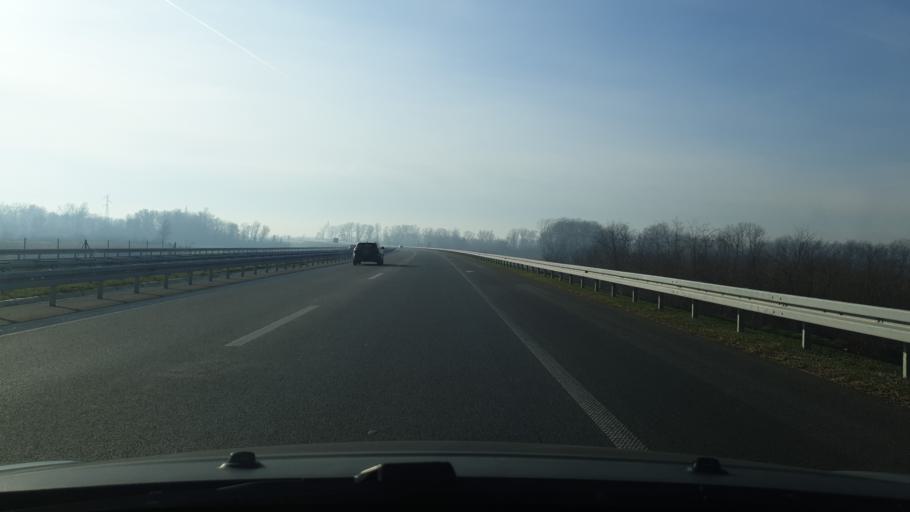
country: RS
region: Central Serbia
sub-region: Belgrade
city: Obrenovac
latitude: 44.6454
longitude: 20.2173
